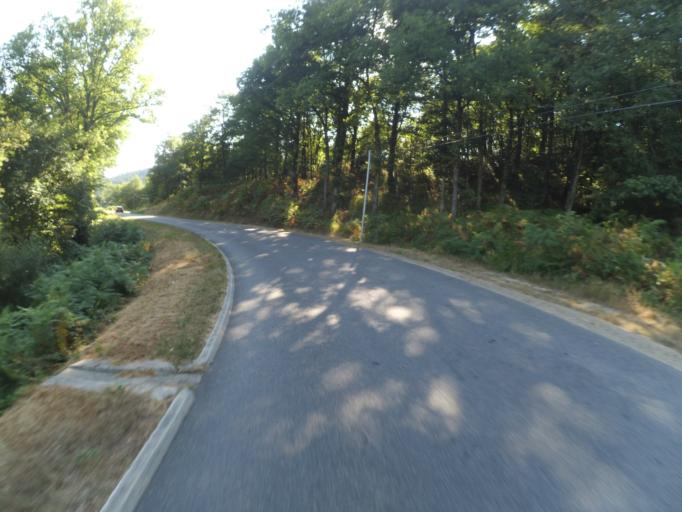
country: FR
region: Limousin
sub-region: Departement de la Haute-Vienne
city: Peyrat-le-Chateau
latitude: 45.7579
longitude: 1.8167
